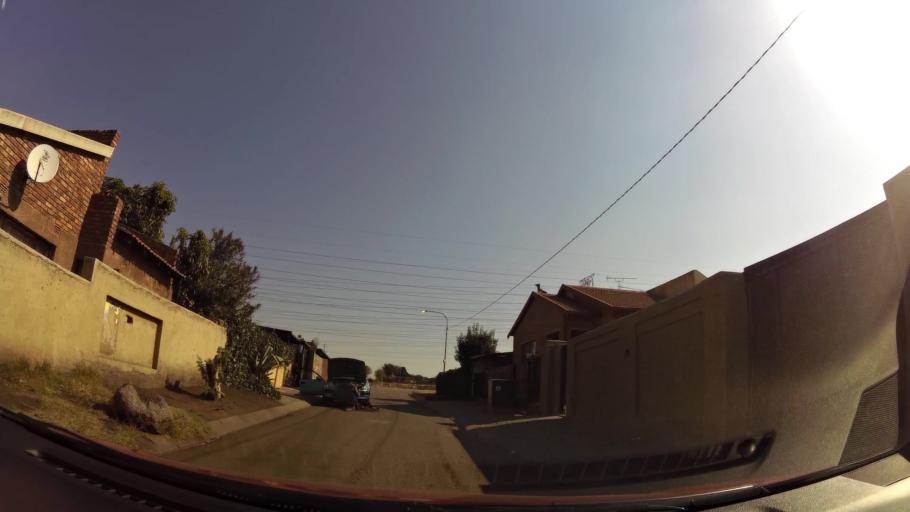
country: ZA
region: Gauteng
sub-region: City of Johannesburg Metropolitan Municipality
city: Soweto
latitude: -26.2484
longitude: 27.9353
